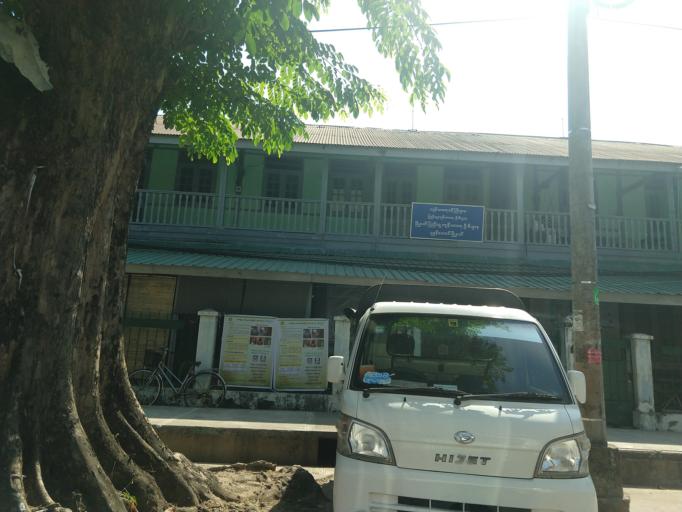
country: MM
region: Yangon
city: Yangon
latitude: 16.7786
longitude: 96.1725
